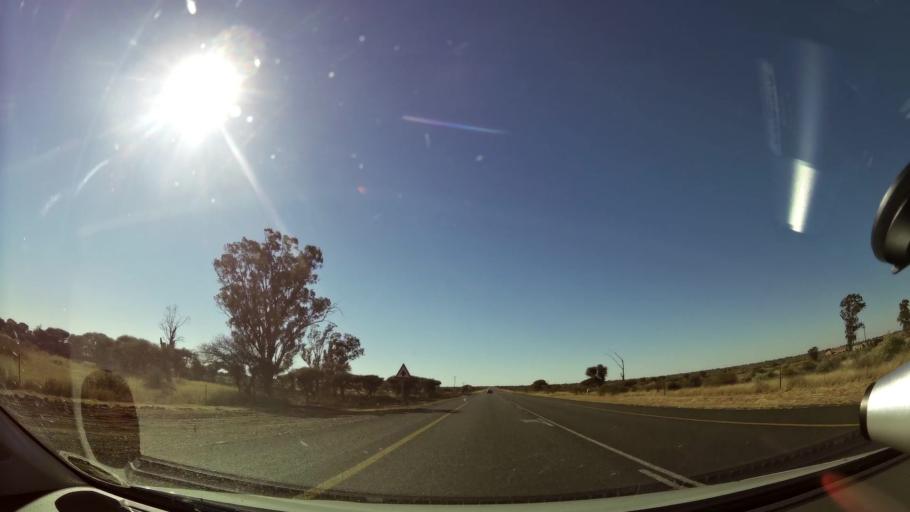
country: ZA
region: Northern Cape
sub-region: Frances Baard District Municipality
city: Warrenton
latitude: -28.0810
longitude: 24.8817
